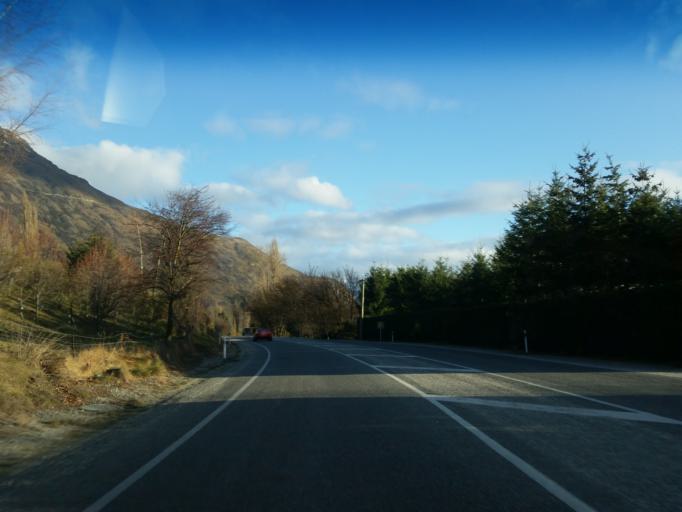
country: NZ
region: Otago
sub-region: Queenstown-Lakes District
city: Arrowtown
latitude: -44.9916
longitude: 168.8078
